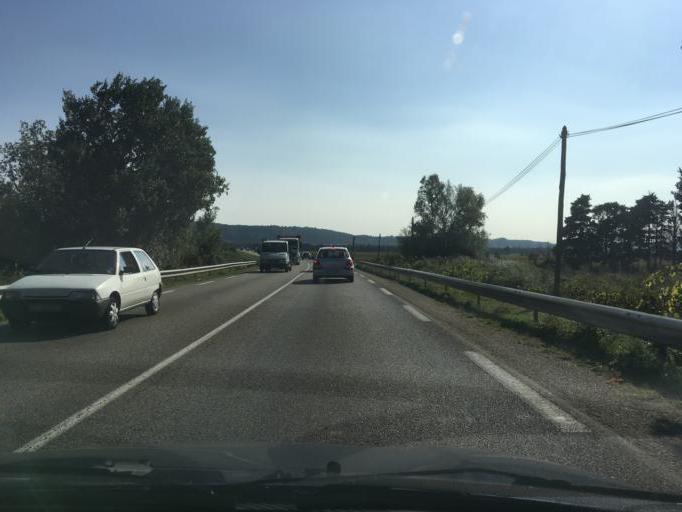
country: FR
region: Languedoc-Roussillon
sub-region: Departement du Gard
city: Pujaut
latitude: 43.9961
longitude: 4.7392
